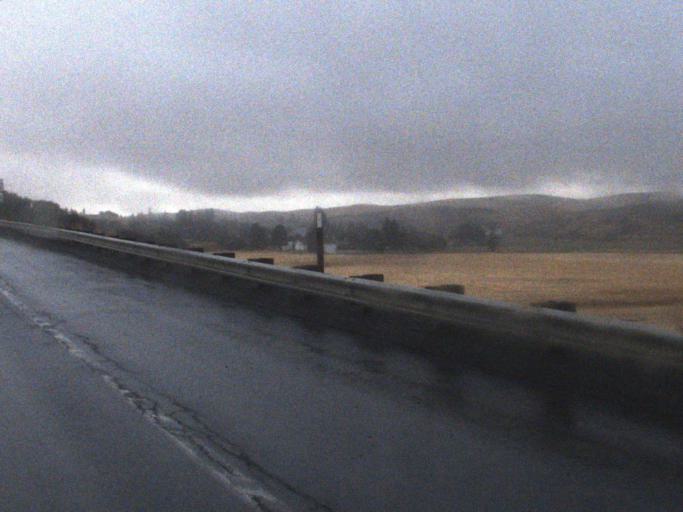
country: US
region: Washington
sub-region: Spokane County
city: Cheney
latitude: 47.2529
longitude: -117.3612
